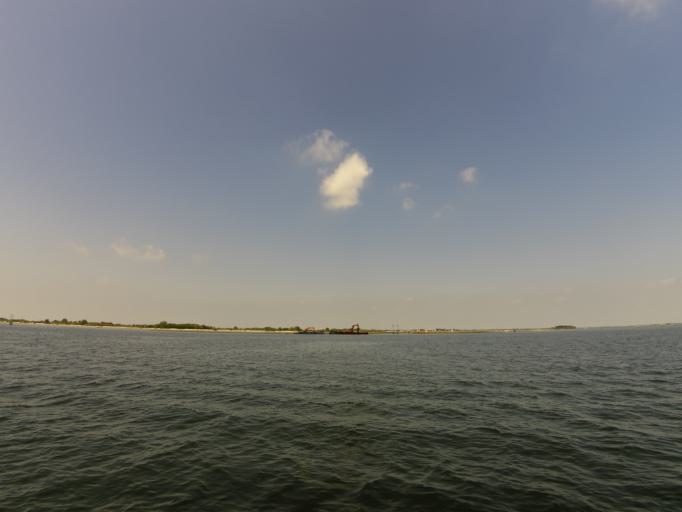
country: IT
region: Veneto
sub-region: Provincia di Venezia
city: Ca' Savio
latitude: 45.4638
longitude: 12.4384
